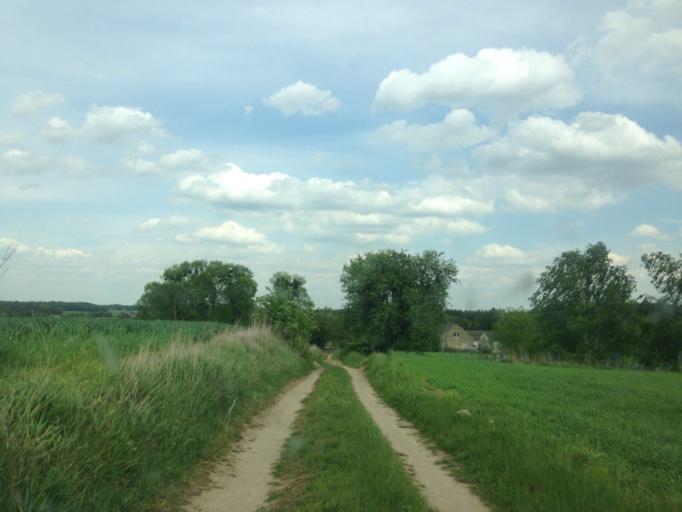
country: PL
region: Kujawsko-Pomorskie
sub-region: Powiat brodnicki
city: Bobrowo
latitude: 53.2501
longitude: 19.2810
